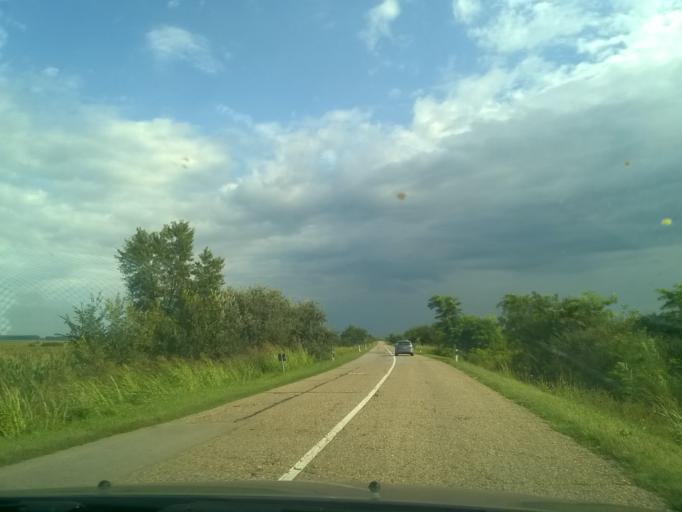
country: RS
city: Uzdin
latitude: 45.1731
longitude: 20.6178
